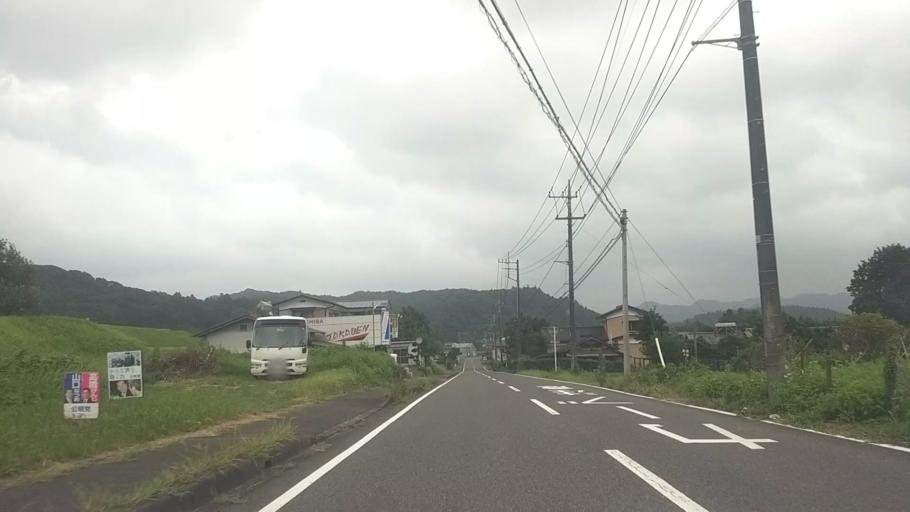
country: JP
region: Chiba
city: Kawaguchi
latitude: 35.2468
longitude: 140.0794
